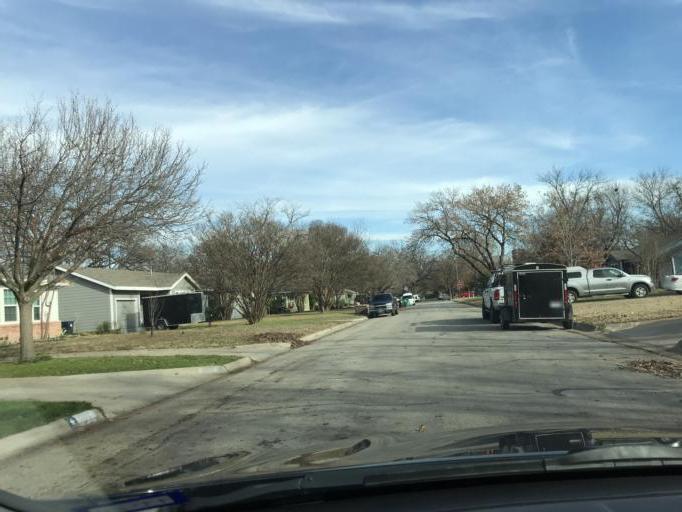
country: US
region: Texas
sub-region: Denton County
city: Denton
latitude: 33.2277
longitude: -97.1414
